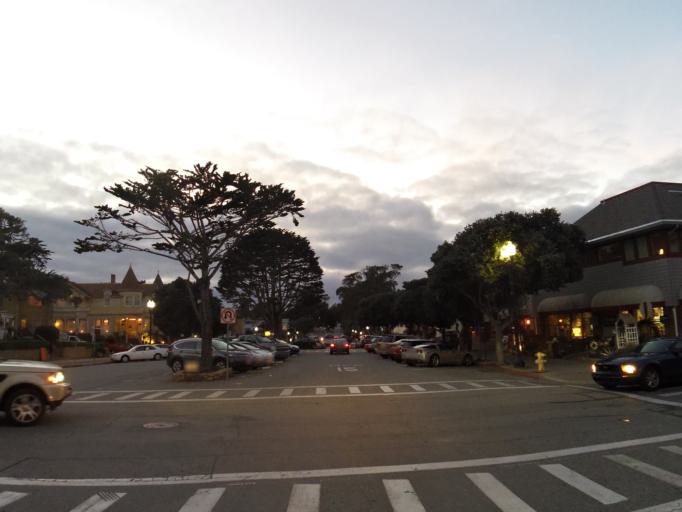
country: US
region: California
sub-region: Monterey County
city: Pacific Grove
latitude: 36.6216
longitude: -121.9187
